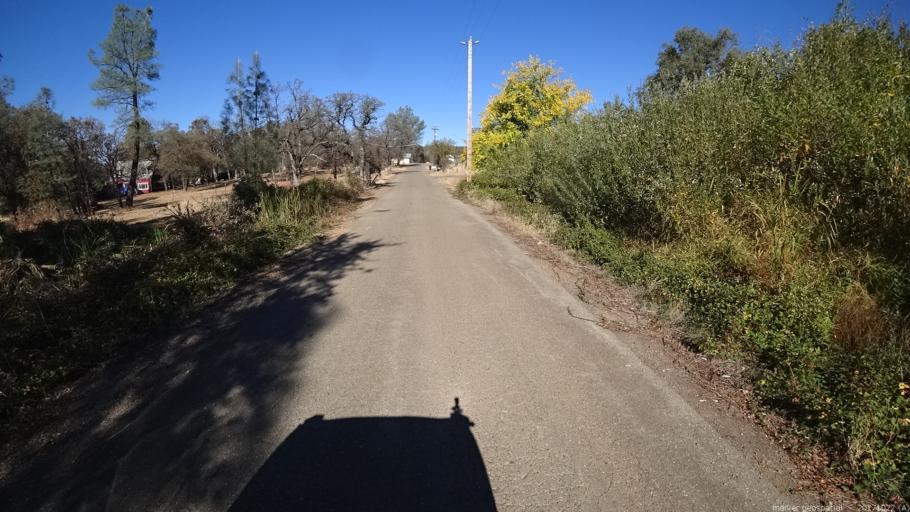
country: US
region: California
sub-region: Shasta County
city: Bella Vista
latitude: 40.6896
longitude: -122.0309
